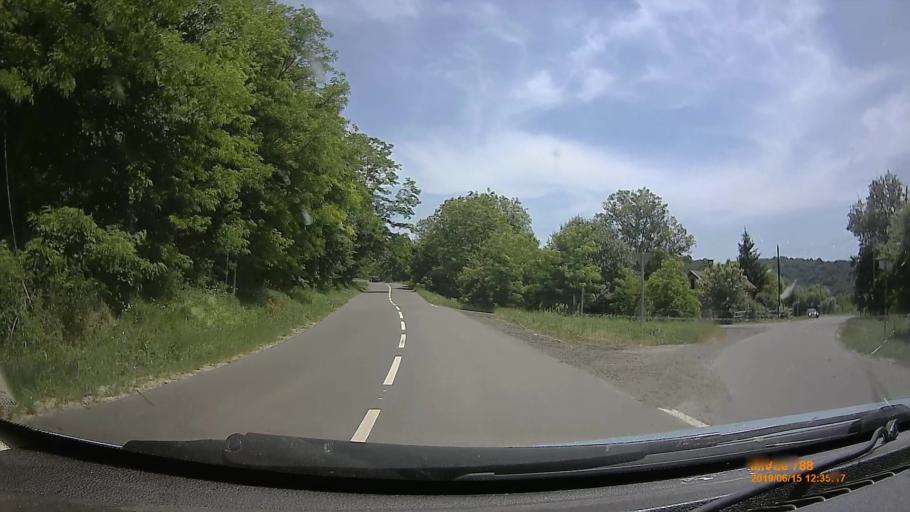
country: HU
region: Baranya
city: Sasd
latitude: 46.1548
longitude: 18.0868
